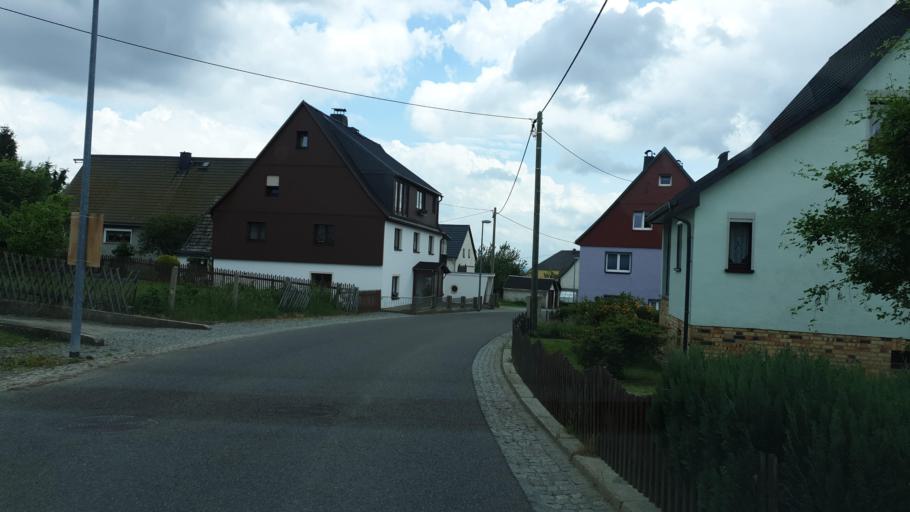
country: DE
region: Saxony
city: Marienberg
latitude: 50.6819
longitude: 13.1645
